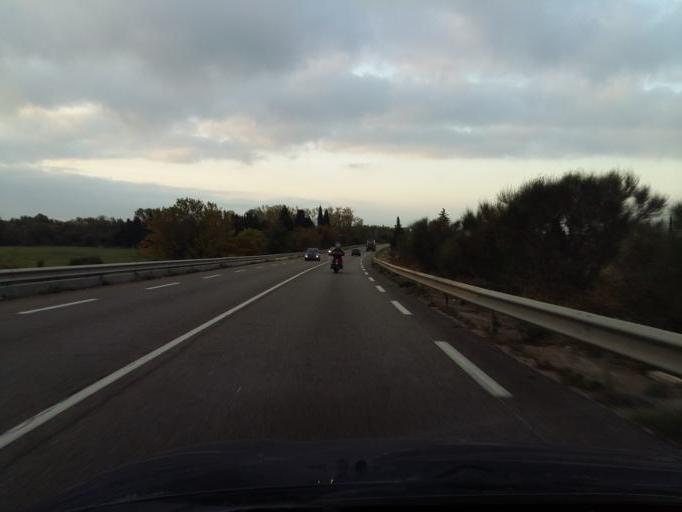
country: FR
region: Provence-Alpes-Cote d'Azur
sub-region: Departement des Bouches-du-Rhone
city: Miramas
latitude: 43.5765
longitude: 4.9841
